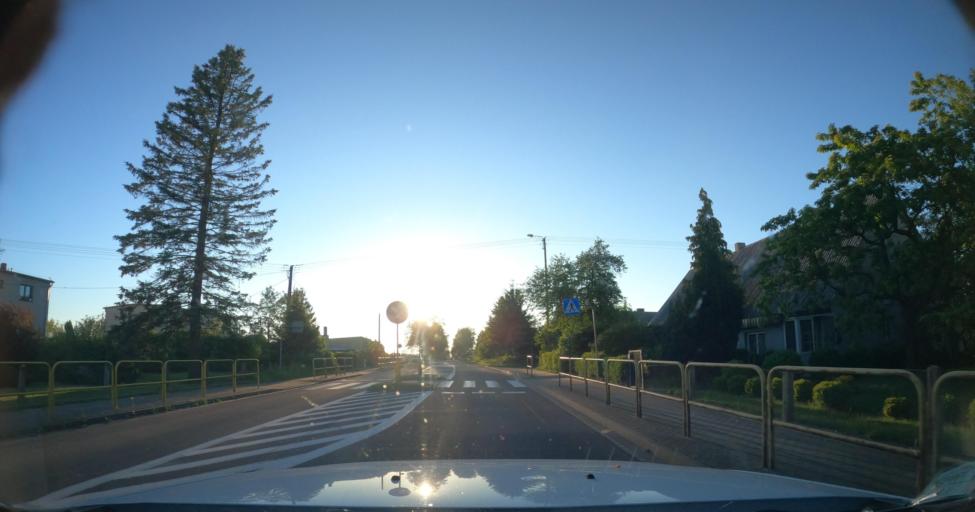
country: PL
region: Pomeranian Voivodeship
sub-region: Powiat slupski
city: Potegowo
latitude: 54.4231
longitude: 17.3786
